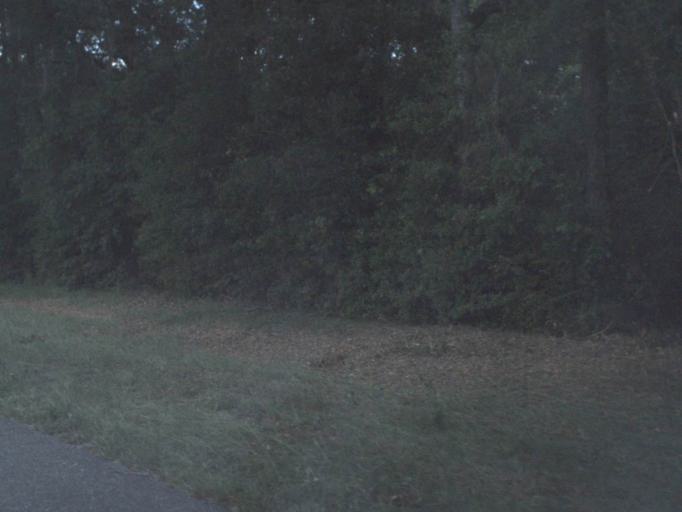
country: US
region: Florida
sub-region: Alachua County
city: High Springs
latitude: 29.8185
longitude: -82.7414
